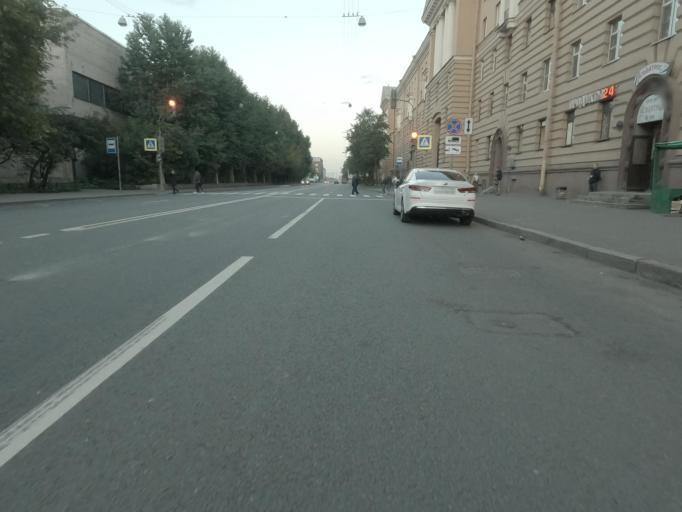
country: RU
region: St.-Petersburg
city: Vasyl'evsky Ostrov
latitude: 59.9091
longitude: 30.2477
